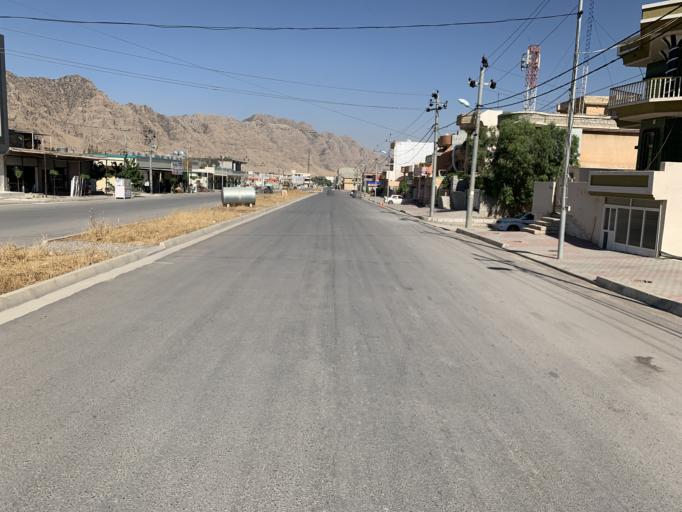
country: IQ
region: As Sulaymaniyah
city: Raniye
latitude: 36.2580
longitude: 44.8701
